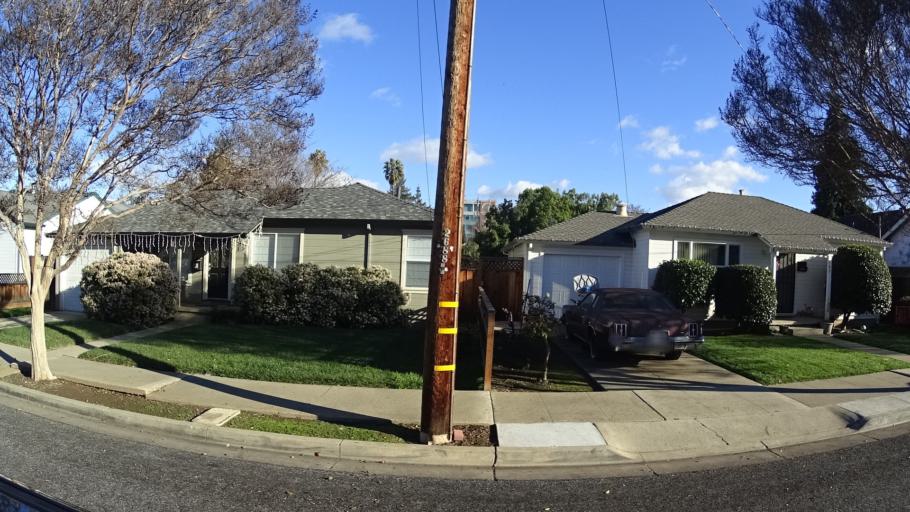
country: US
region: California
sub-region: Santa Clara County
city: Sunnyvale
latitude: 37.3785
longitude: -122.0361
